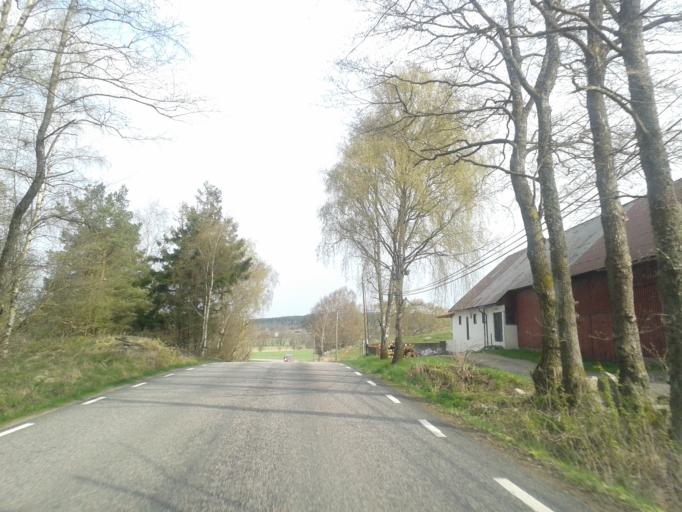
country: SE
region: Vaestra Goetaland
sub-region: Kungalvs Kommun
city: Kode
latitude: 57.9056
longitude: 11.8047
